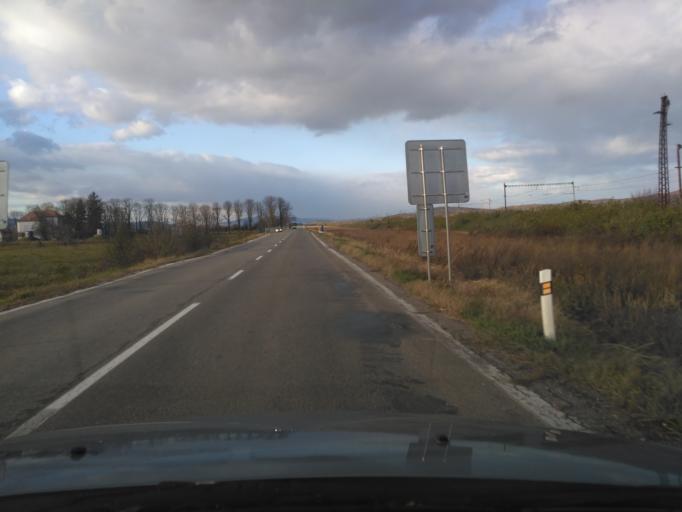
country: HU
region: Borsod-Abauj-Zemplen
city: Satoraljaujhely
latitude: 48.4135
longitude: 21.6653
